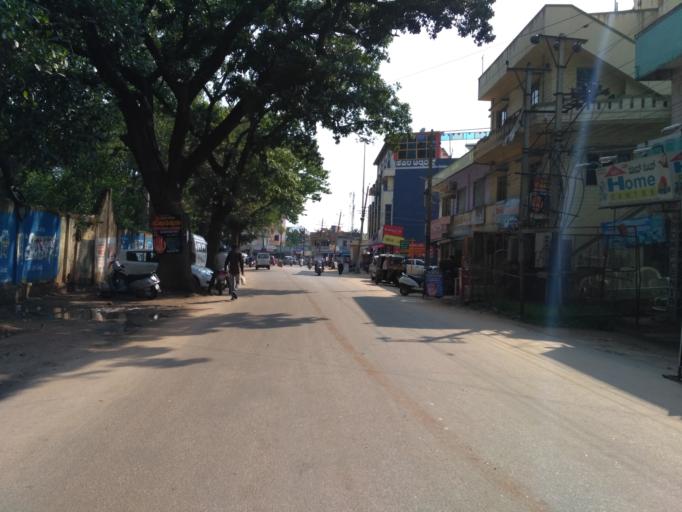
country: IN
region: Karnataka
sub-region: Hassan
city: Hassan
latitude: 13.0102
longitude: 76.1040
